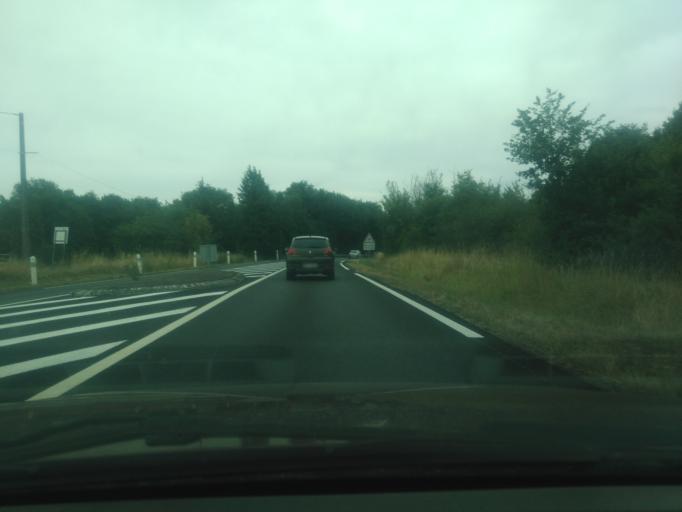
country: FR
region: Poitou-Charentes
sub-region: Departement de la Vienne
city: Chauvigny
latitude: 46.5686
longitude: 0.6599
